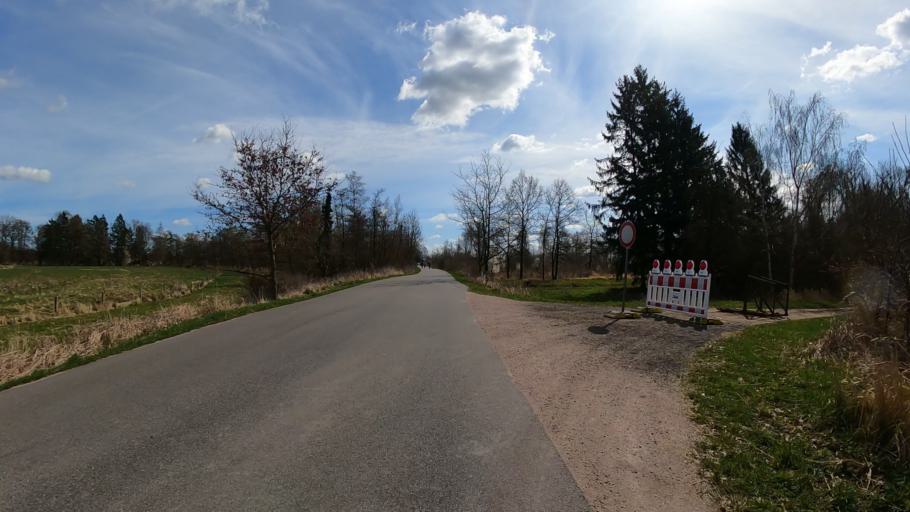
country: DE
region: Lower Saxony
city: Winsen
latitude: 53.4036
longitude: 10.2166
